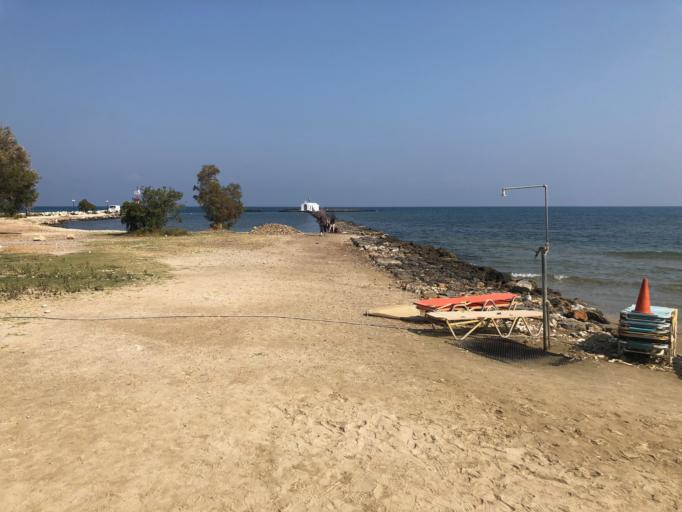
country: GR
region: Crete
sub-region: Nomos Chanias
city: Georgioupolis
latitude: 35.3634
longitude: 24.2620
